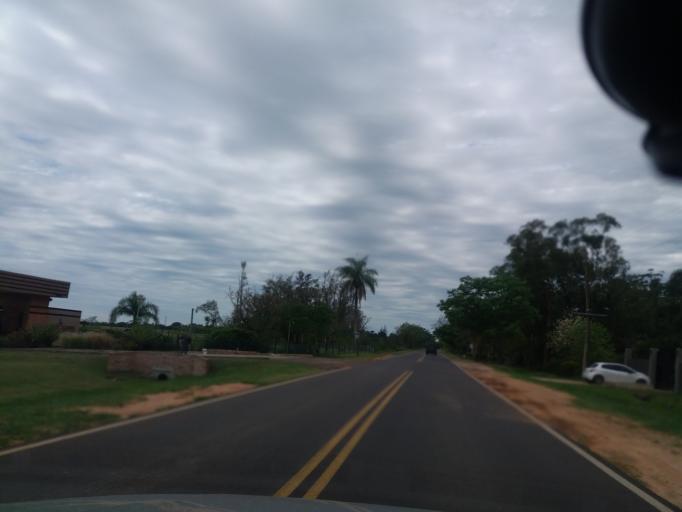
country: AR
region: Corrientes
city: Corrientes
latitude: -27.4565
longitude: -58.7143
